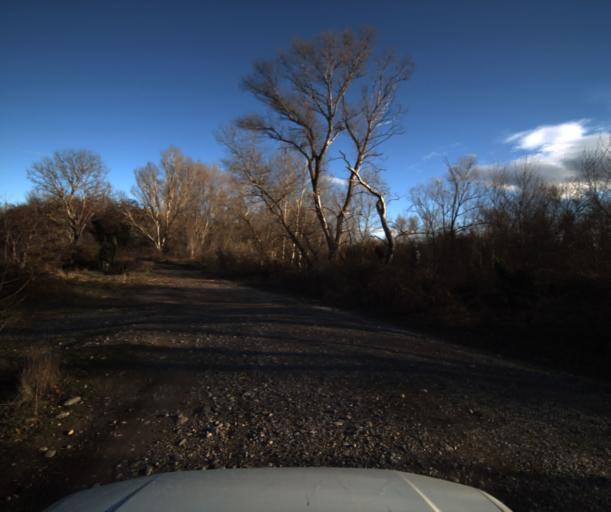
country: FR
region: Provence-Alpes-Cote d'Azur
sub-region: Departement du Vaucluse
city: Pertuis
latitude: 43.6734
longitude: 5.4742
